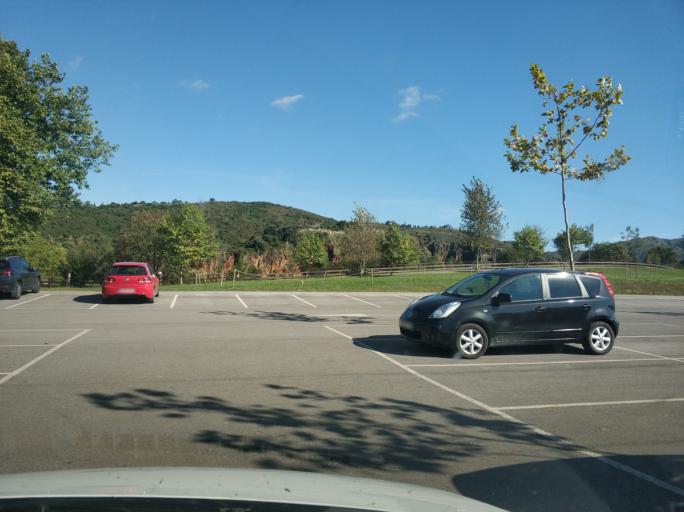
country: ES
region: Cantabria
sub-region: Provincia de Cantabria
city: Penagos
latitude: 43.3504
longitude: -3.8428
